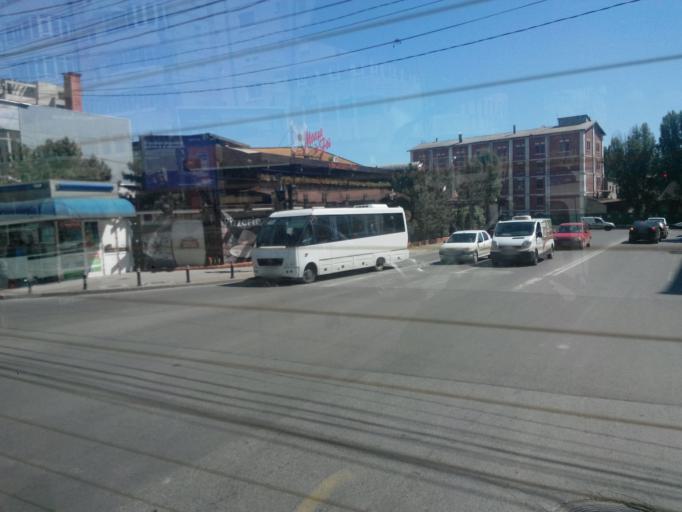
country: RO
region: Iasi
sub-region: Comuna Miroslava
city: Miroslava
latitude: 47.1744
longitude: 27.5515
